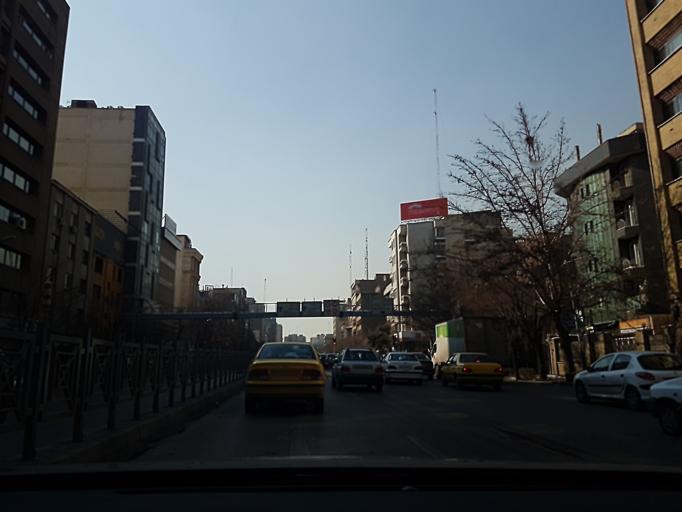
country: IR
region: Tehran
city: Tehran
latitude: 35.7154
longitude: 51.4215
